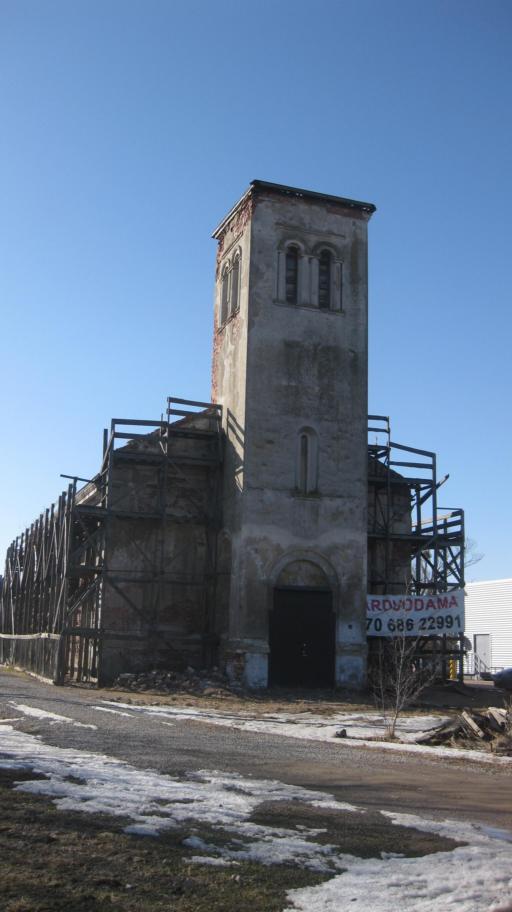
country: LT
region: Kauno apskritis
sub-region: Kauno rajonas
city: Garliava
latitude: 54.8256
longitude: 23.8729
